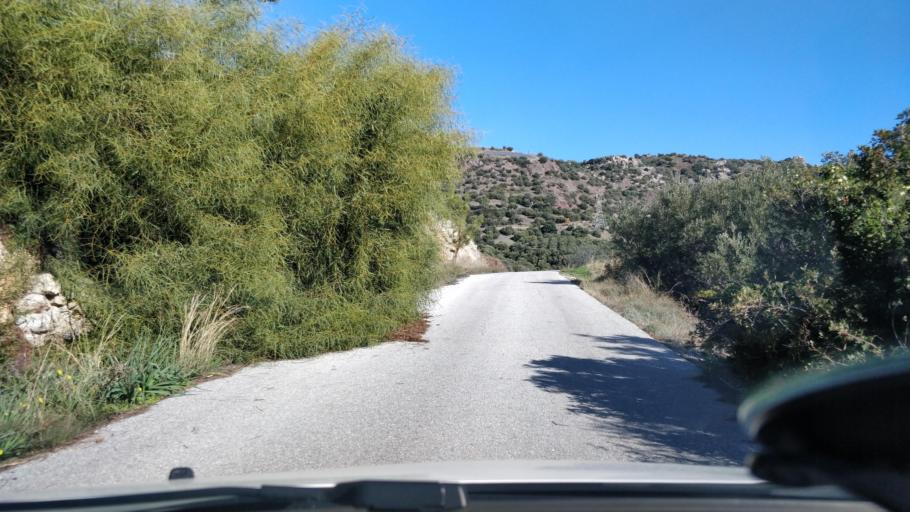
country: GR
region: Crete
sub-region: Nomos Lasithiou
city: Gra Liyia
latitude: 35.0195
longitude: 25.5514
